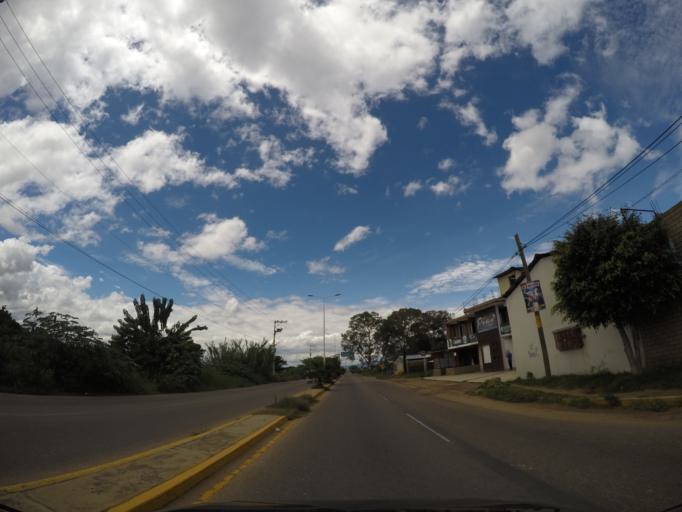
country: MX
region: Oaxaca
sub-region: Santa Cruz Xoxocotlan
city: San Isidro Monjas
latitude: 17.0022
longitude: -96.7394
